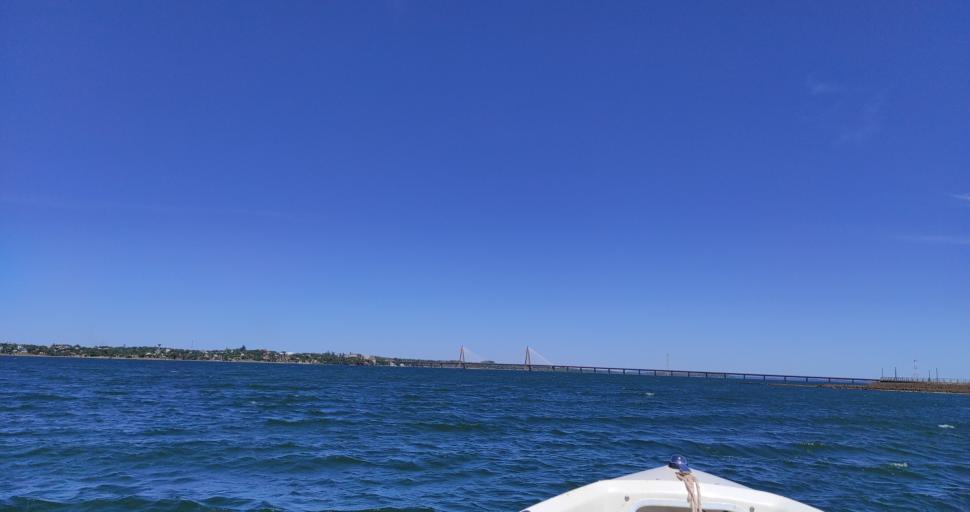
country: AR
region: Misiones
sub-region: Departamento de Capital
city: Posadas
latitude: -27.3597
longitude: -55.8866
